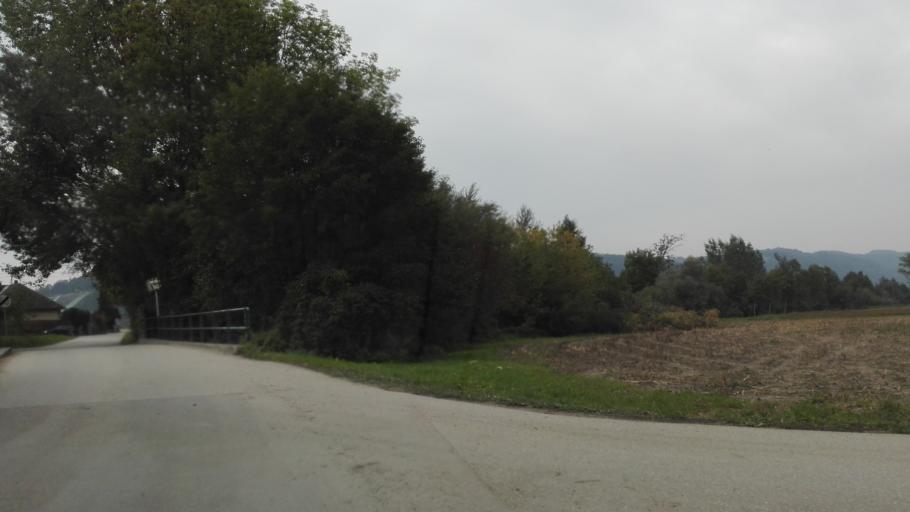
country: AT
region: Upper Austria
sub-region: Politischer Bezirk Urfahr-Umgebung
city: Feldkirchen an der Donau
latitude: 48.3294
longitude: 14.0115
